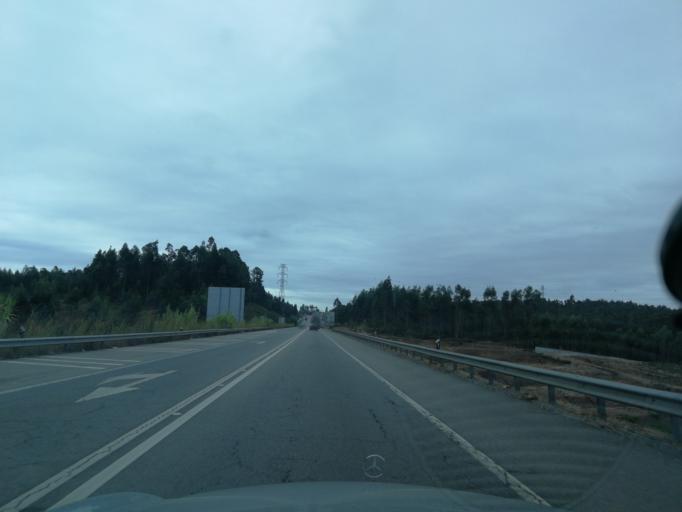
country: PT
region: Aveiro
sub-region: Agueda
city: Valongo
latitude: 40.6056
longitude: -8.4670
